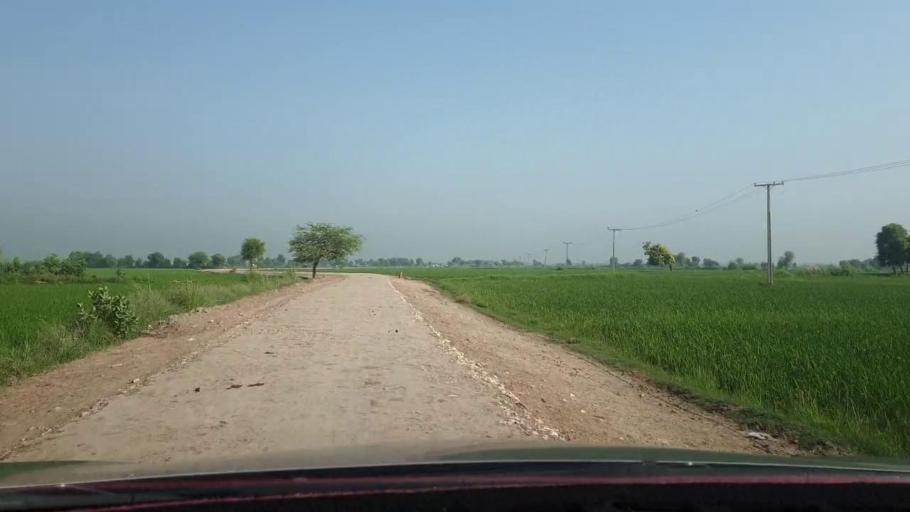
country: PK
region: Sindh
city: Nasirabad
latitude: 27.4281
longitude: 67.9215
